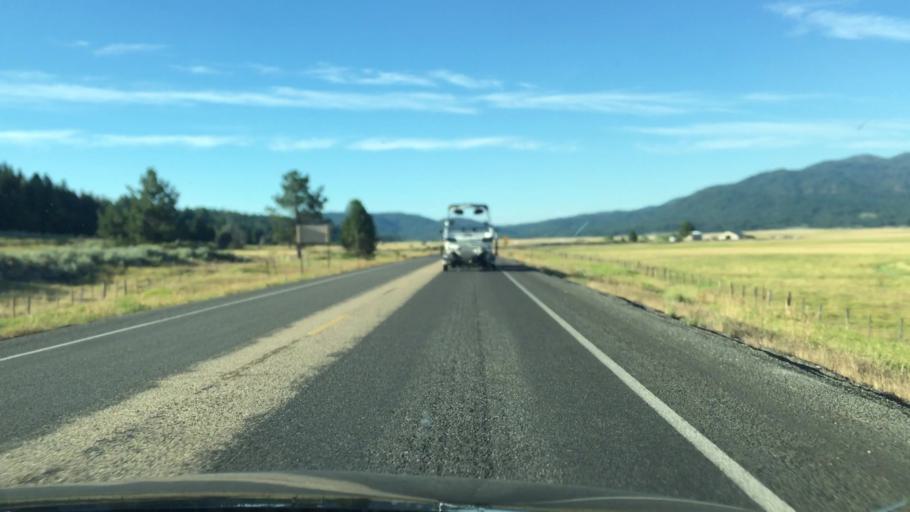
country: US
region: Idaho
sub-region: Valley County
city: Cascade
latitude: 44.5344
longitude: -116.0367
